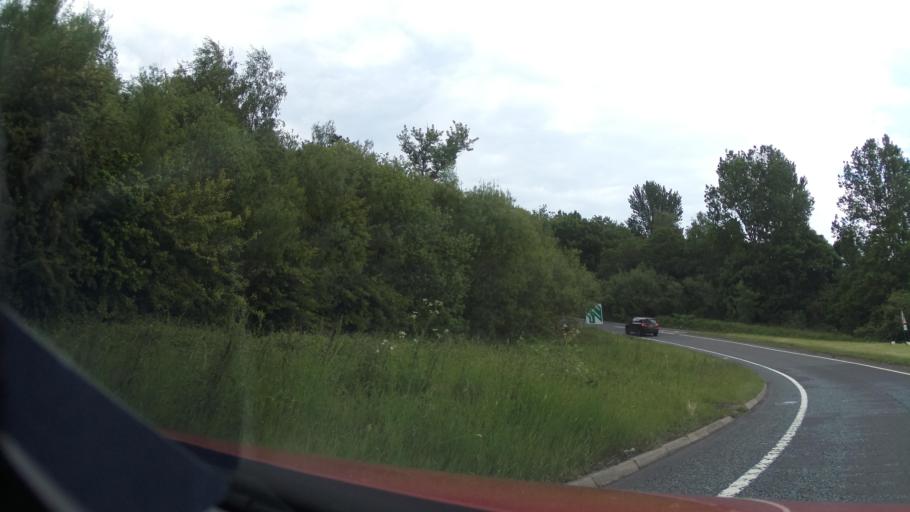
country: GB
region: England
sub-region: County Durham
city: Chester-le-Street
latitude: 54.9023
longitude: -1.5637
